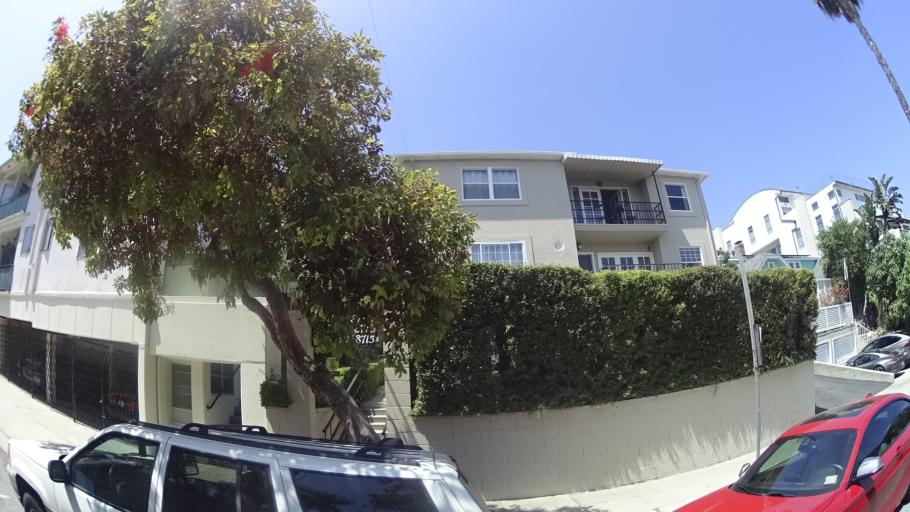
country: US
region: California
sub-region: Los Angeles County
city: West Hollywood
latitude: 34.0894
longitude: -118.3809
